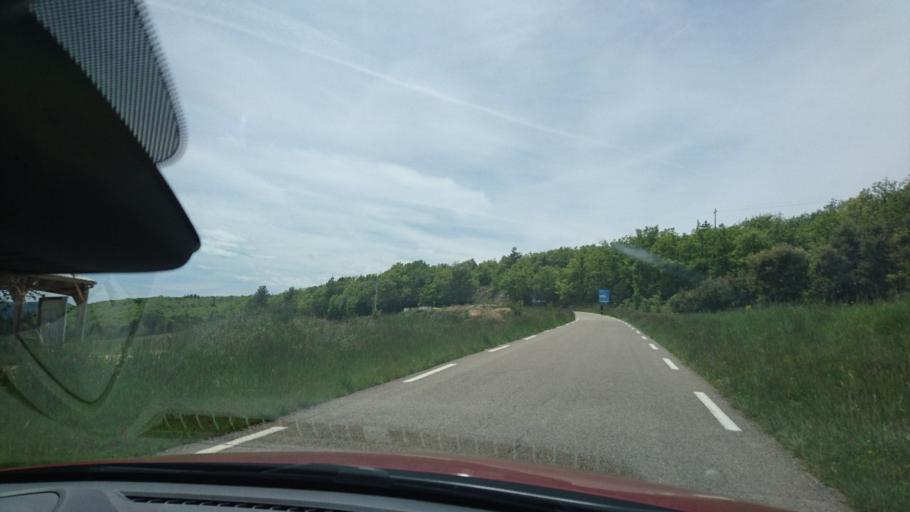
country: FR
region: Provence-Alpes-Cote d'Azur
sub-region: Departement du Vaucluse
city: Sault
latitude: 44.1143
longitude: 5.3961
